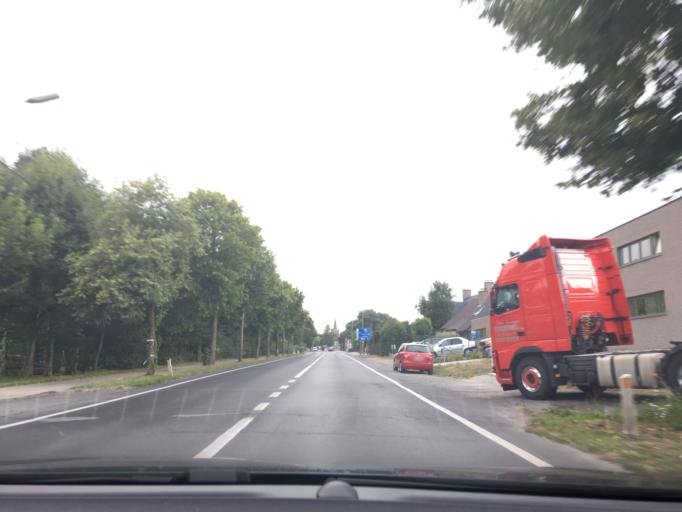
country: BE
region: Flanders
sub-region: Provincie West-Vlaanderen
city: Staden
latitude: 50.9362
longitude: 3.0193
